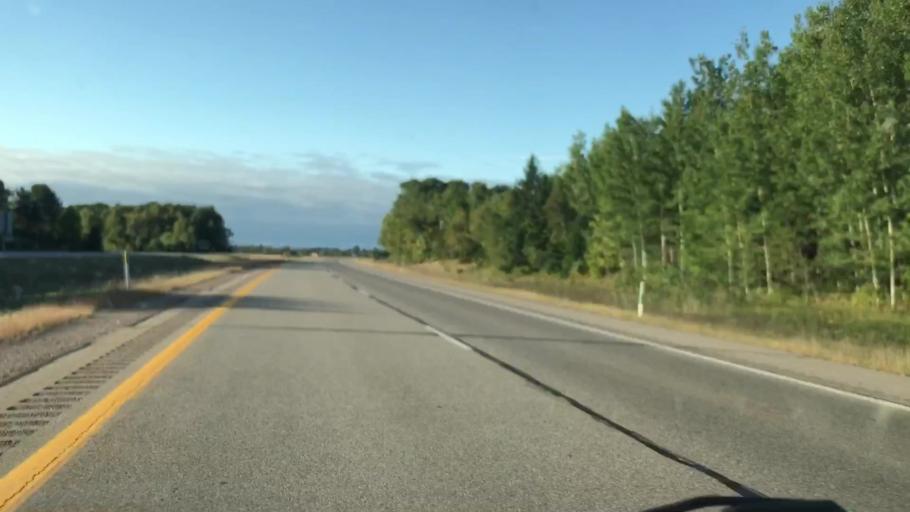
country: US
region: Michigan
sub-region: Chippewa County
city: Sault Ste. Marie
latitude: 46.4499
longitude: -84.3840
